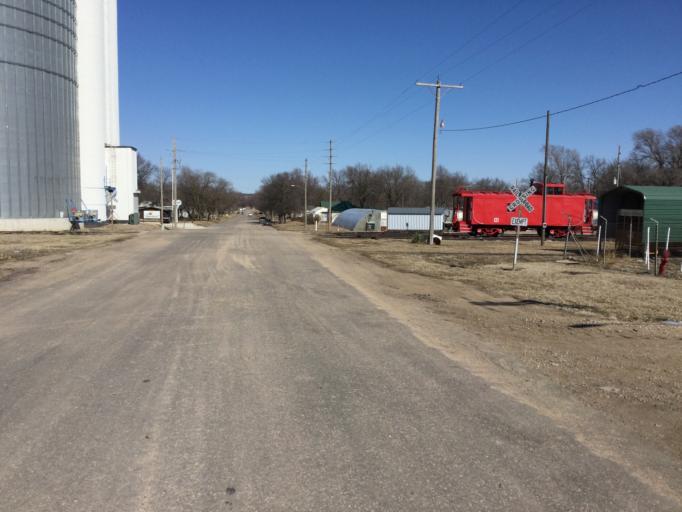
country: US
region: Kansas
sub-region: Marshall County
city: Blue Rapids
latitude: 39.6745
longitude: -96.6593
